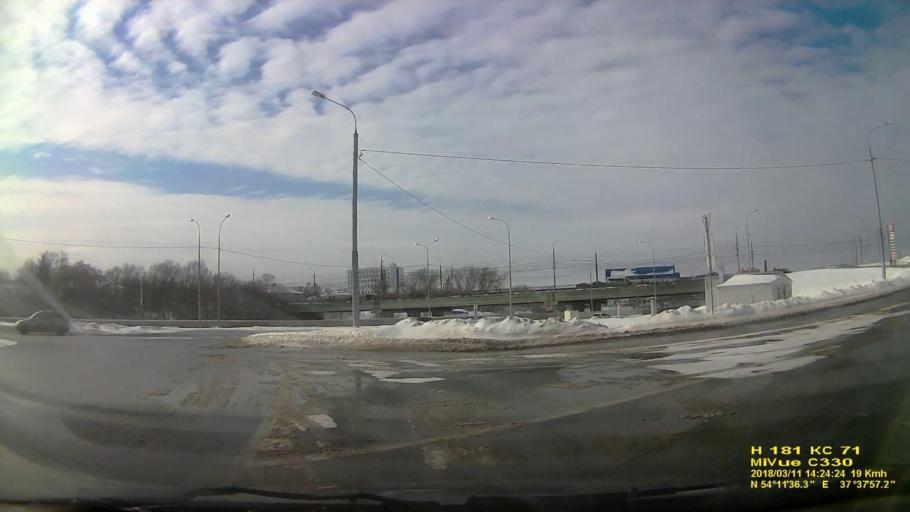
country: RU
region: Tula
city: Tula
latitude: 54.1935
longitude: 37.6327
